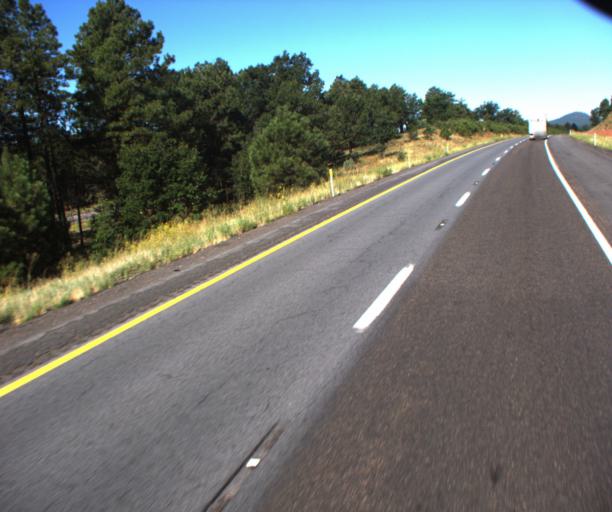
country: US
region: Arizona
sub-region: Coconino County
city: Parks
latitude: 35.2531
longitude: -111.9083
